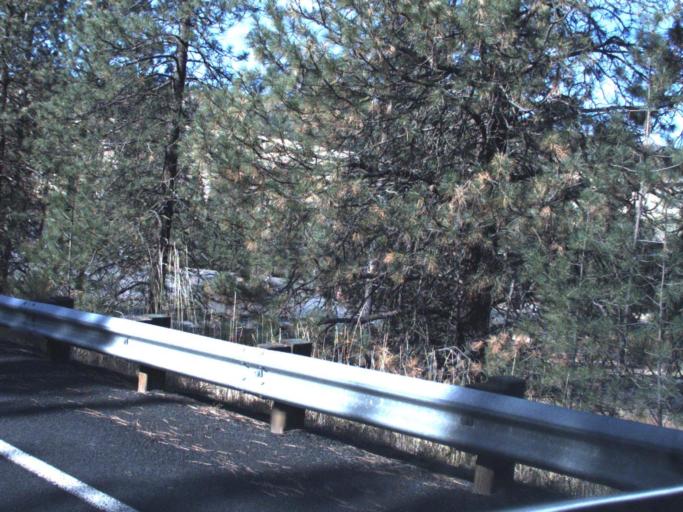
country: US
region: Washington
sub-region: Lincoln County
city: Davenport
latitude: 47.9082
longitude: -118.3091
